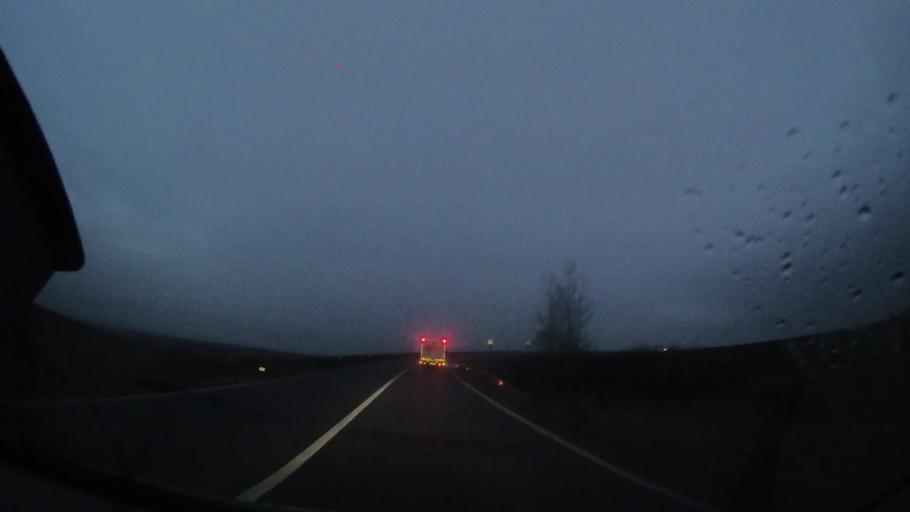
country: RO
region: Harghita
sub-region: Comuna Subcetate
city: Subcetate
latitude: 46.8404
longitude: 25.4770
